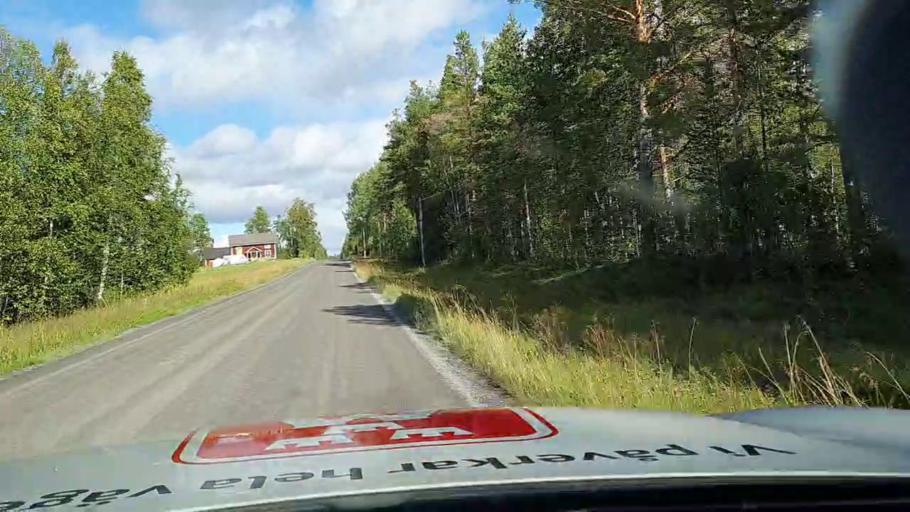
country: SE
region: Jaemtland
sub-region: Stroemsunds Kommun
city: Stroemsund
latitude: 63.6848
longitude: 15.1196
